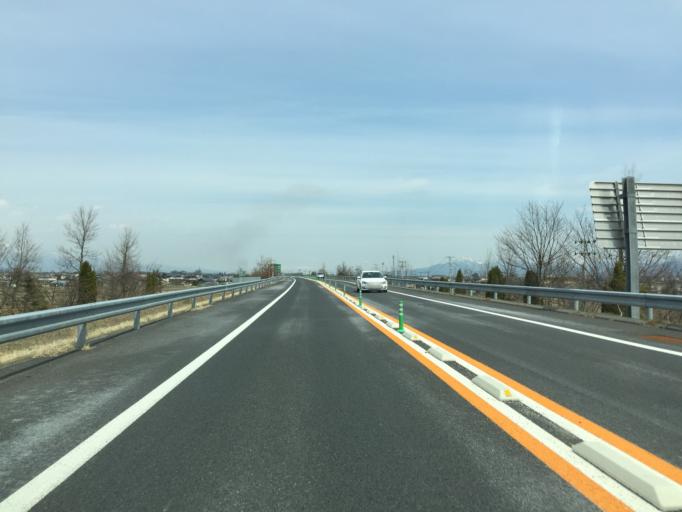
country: JP
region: Yamagata
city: Yamagata-shi
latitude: 38.2797
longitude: 140.2972
